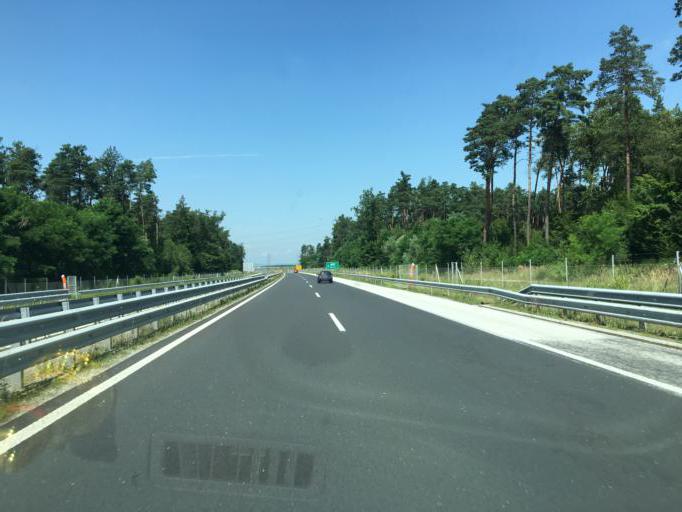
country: SI
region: Kidricevo
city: Kidricevo
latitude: 46.4358
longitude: 15.7885
